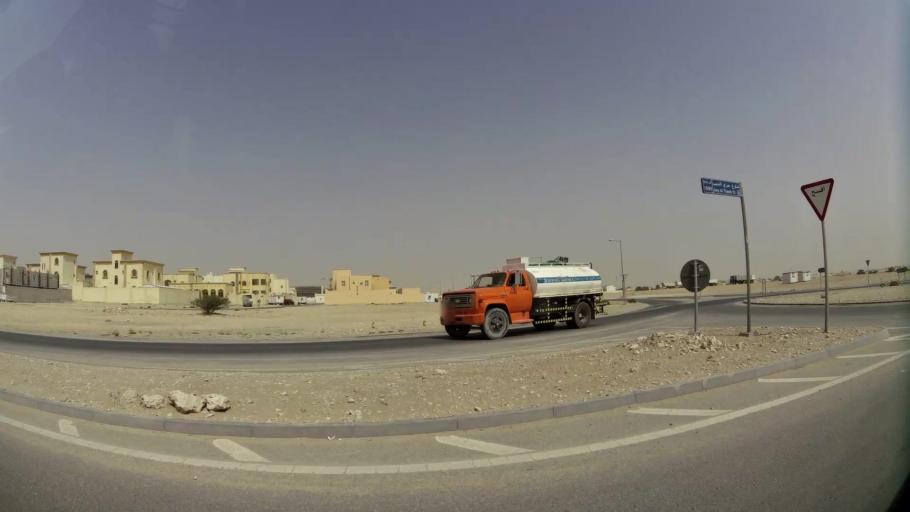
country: QA
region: Baladiyat ar Rayyan
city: Ar Rayyan
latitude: 25.2368
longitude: 51.3667
